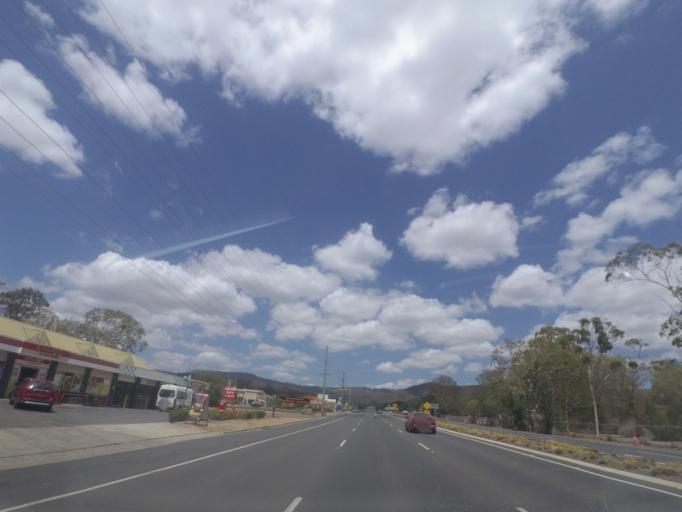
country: AU
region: Queensland
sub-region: Toowoomba
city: East Toowoomba
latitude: -27.5529
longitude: 152.0272
